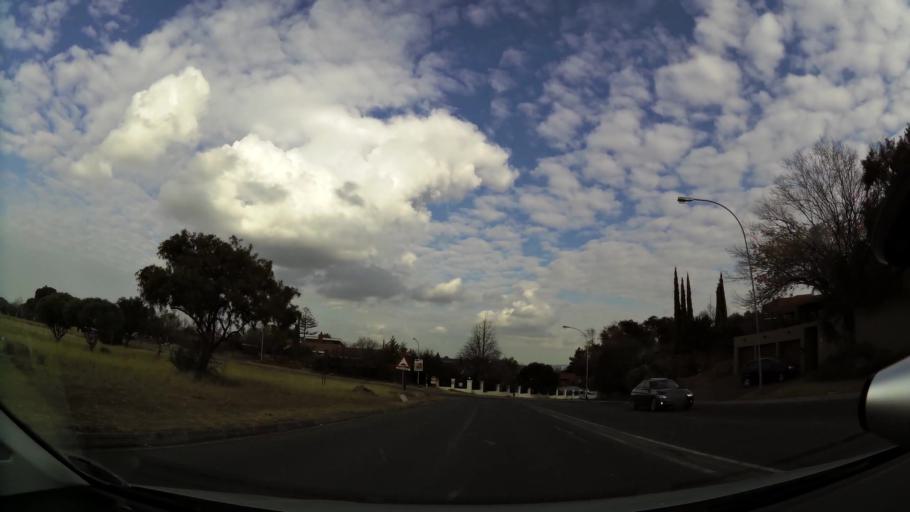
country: ZA
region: Orange Free State
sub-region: Mangaung Metropolitan Municipality
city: Bloemfontein
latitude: -29.0828
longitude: 26.2033
